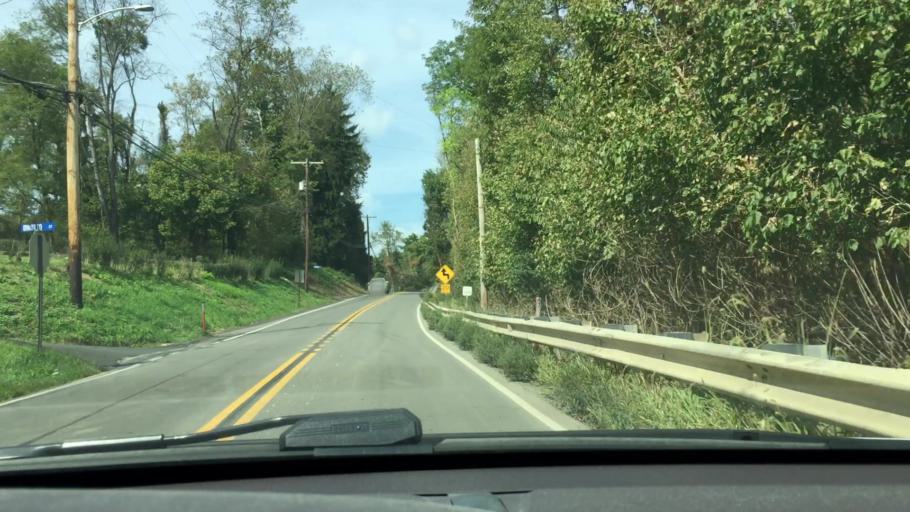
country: US
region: Pennsylvania
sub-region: Washington County
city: Thompsonville
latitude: 40.3032
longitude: -80.1156
